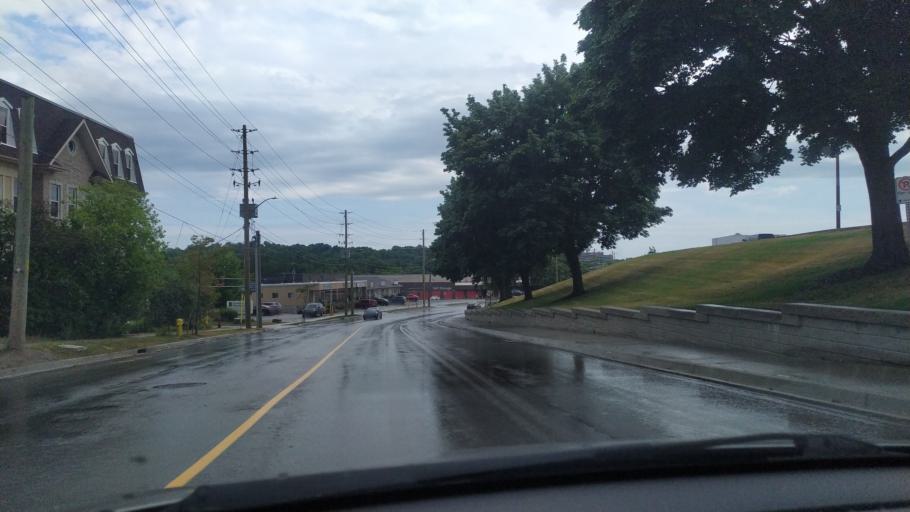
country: CA
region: Ontario
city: Waterloo
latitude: 43.4833
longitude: -80.5182
